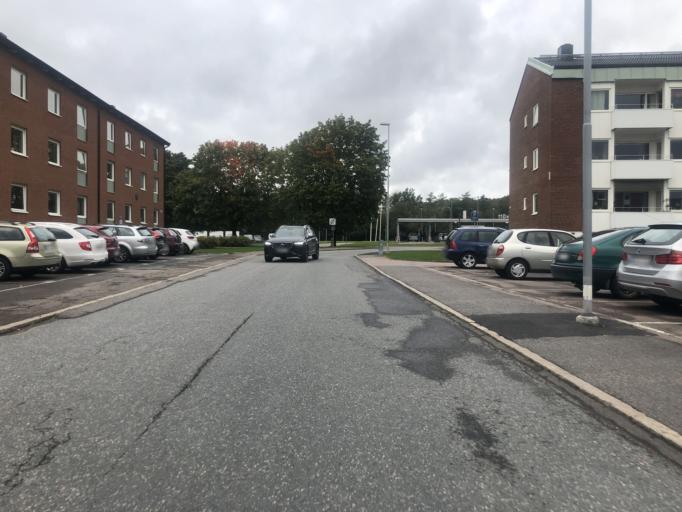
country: SE
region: Vaestra Goetaland
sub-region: Molndal
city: Moelndal
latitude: 57.6600
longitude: 11.9994
